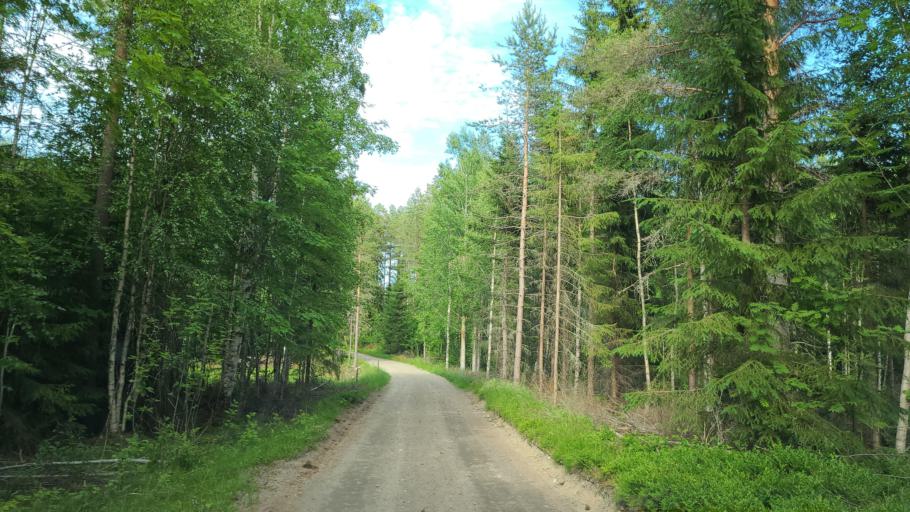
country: SE
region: Vaesterbotten
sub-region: Robertsfors Kommun
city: Robertsfors
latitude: 64.1533
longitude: 20.9209
